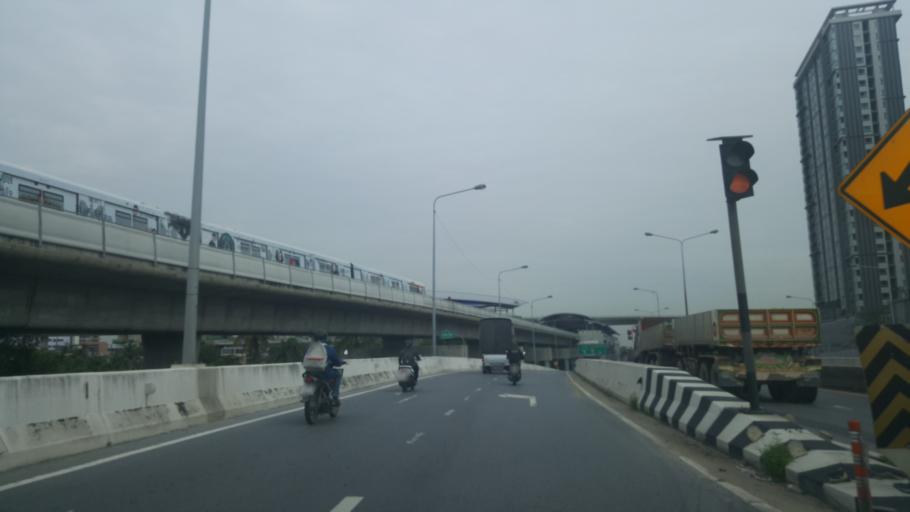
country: TH
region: Bangkok
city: Bangkok Yai
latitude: 13.7181
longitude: 100.4584
